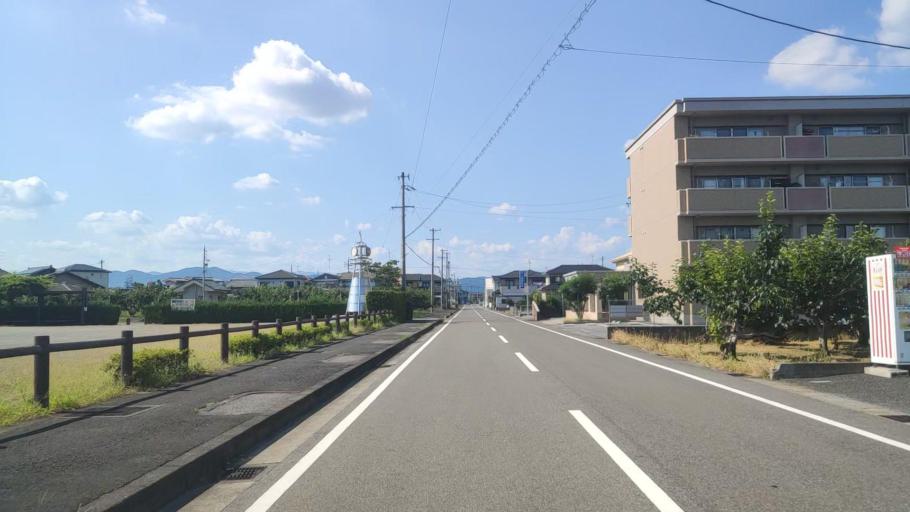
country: JP
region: Gifu
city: Godo
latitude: 35.4469
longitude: 136.6767
